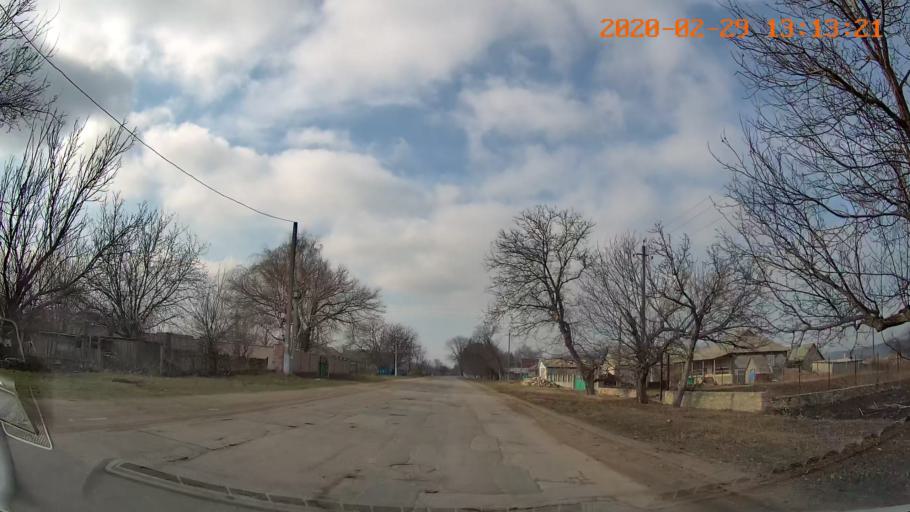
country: MD
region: Telenesti
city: Camenca
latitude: 48.0142
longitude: 28.6852
